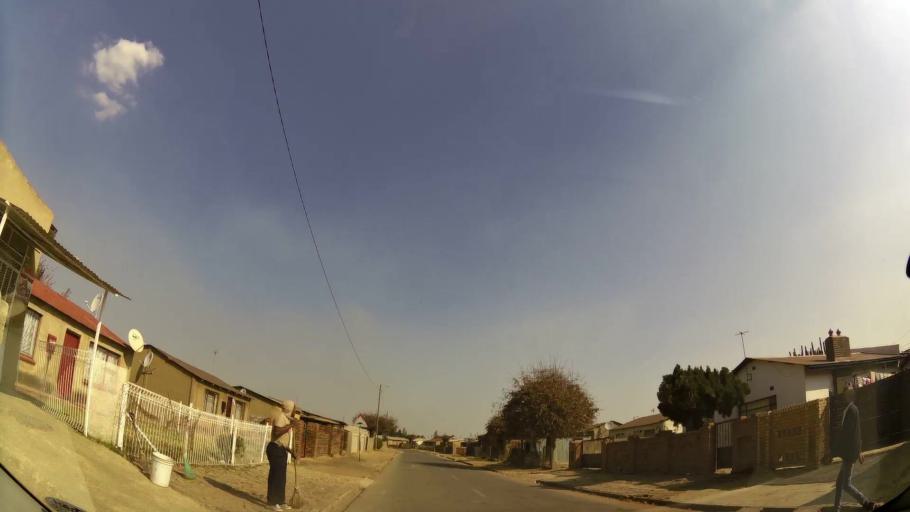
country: ZA
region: Gauteng
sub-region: Ekurhuleni Metropolitan Municipality
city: Brakpan
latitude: -26.1343
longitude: 28.4317
